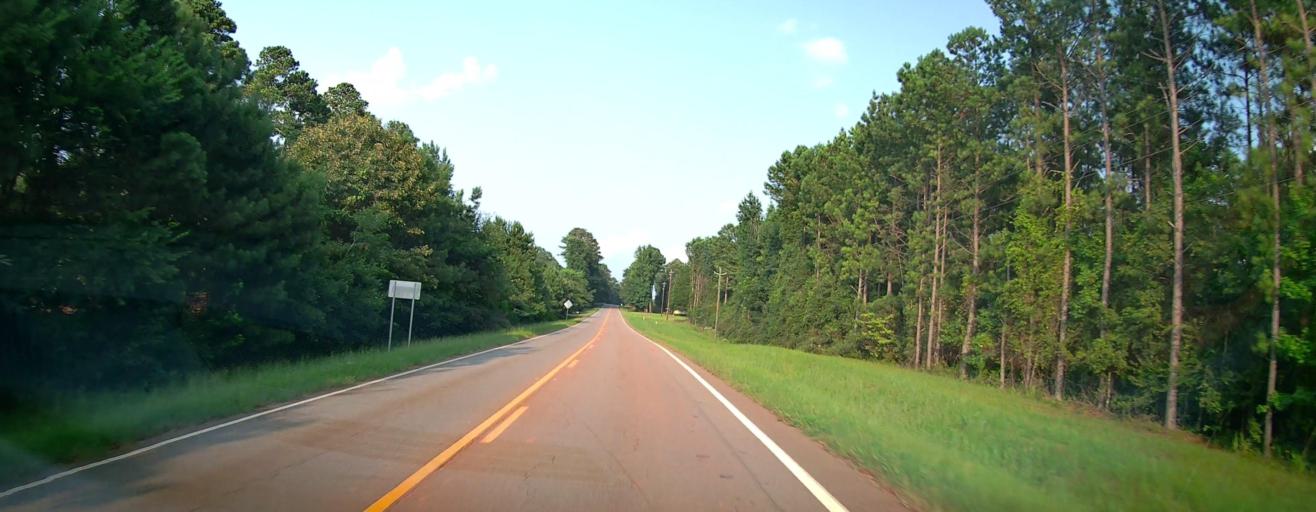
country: US
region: Georgia
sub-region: Jones County
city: Gray
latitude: 33.0594
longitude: -83.6012
